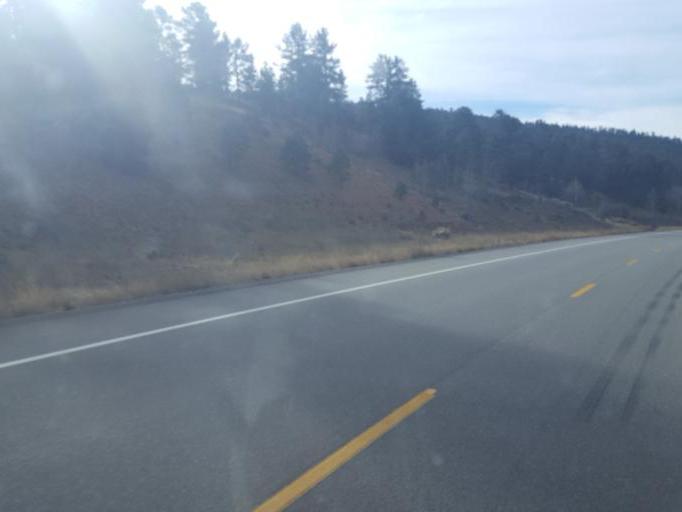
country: US
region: Colorado
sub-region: Costilla County
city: San Luis
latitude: 37.5487
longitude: -105.2842
